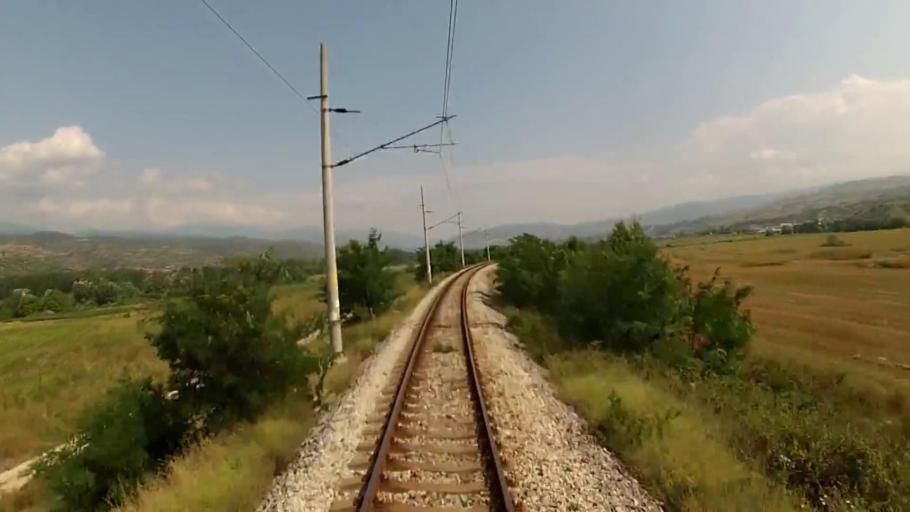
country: BG
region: Blagoevgrad
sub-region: Obshtina Strumyani
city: Strumyani
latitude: 41.6481
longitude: 23.1947
